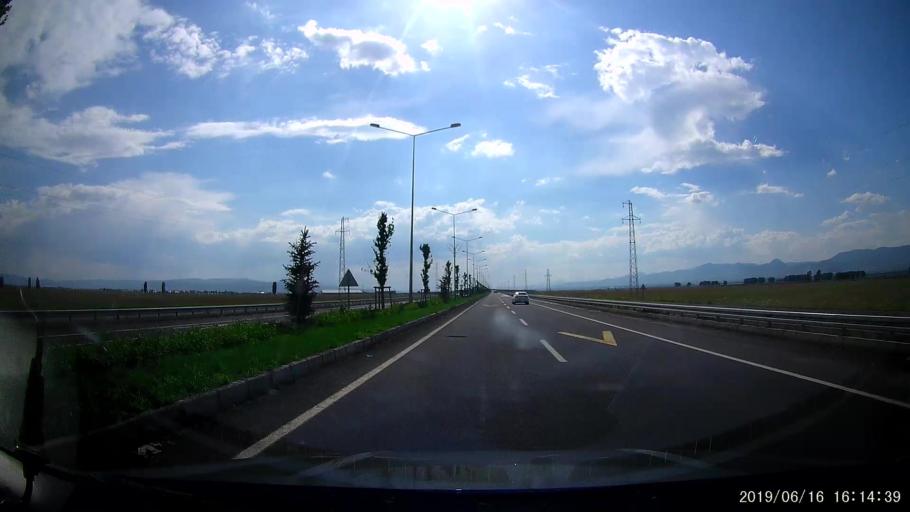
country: TR
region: Erzurum
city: Erzurum
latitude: 39.9610
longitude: 41.2435
